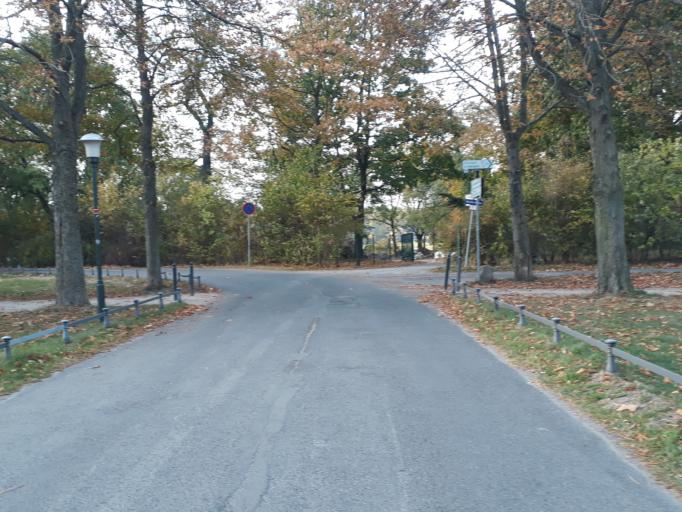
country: DE
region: Saxony
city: Heidenau
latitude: 51.0124
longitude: 13.8642
